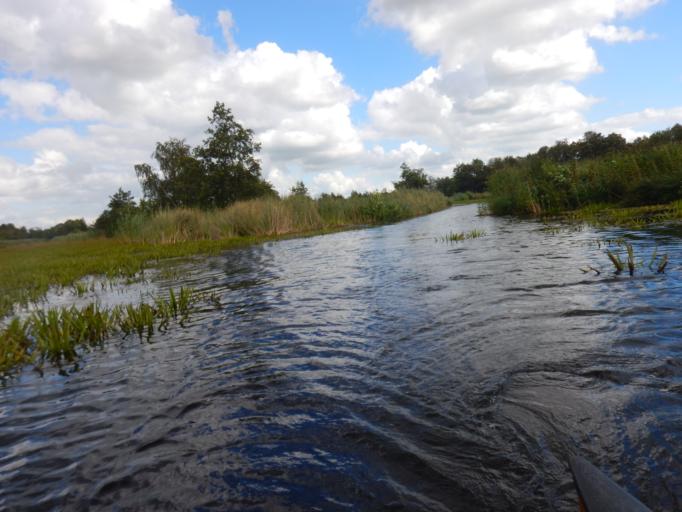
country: NL
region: Overijssel
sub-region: Gemeente Steenwijkerland
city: Blokzijl
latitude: 52.7705
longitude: 5.9475
